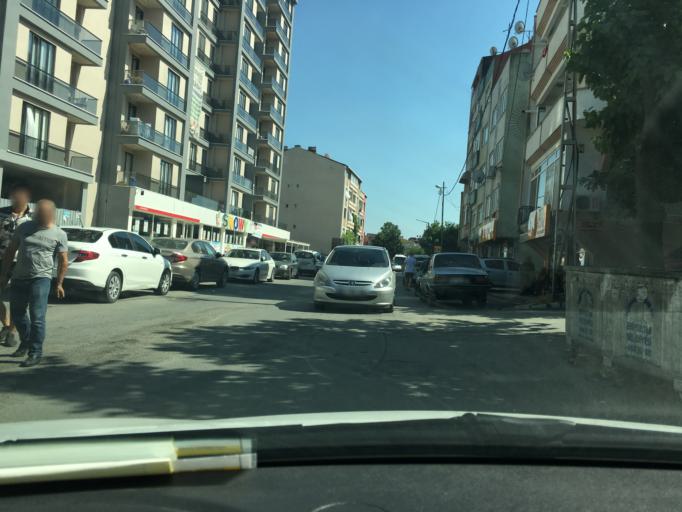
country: TR
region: Istanbul
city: Sisli
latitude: 41.0813
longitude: 28.9440
